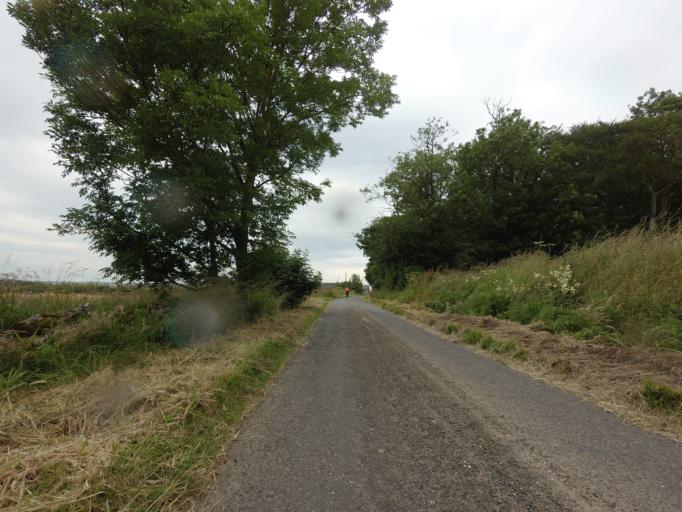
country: GB
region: Scotland
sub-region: Aberdeenshire
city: Portsoy
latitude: 57.6766
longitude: -2.6616
